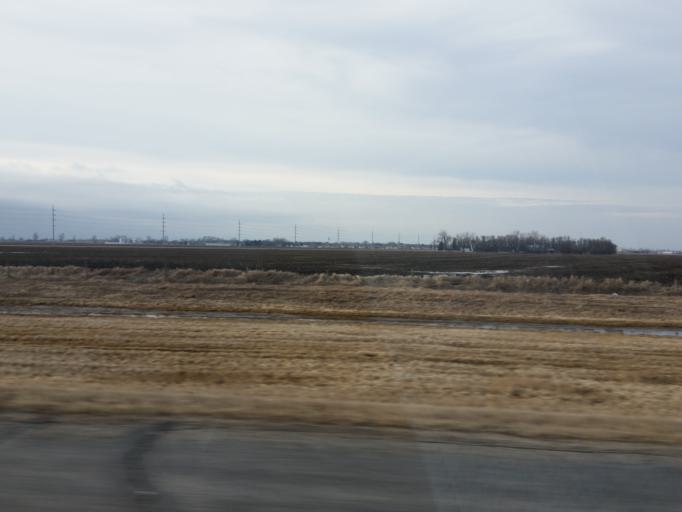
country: US
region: North Dakota
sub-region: Cass County
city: Casselton
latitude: 46.8760
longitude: -97.1972
